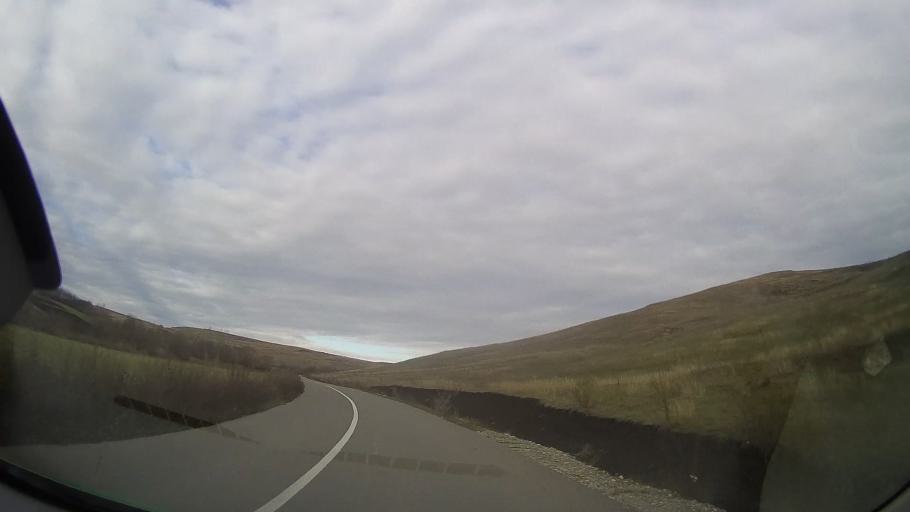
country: RO
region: Bistrita-Nasaud
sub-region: Comuna Silvasu de Campie
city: Silvasu de Campie
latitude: 46.8063
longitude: 24.2969
